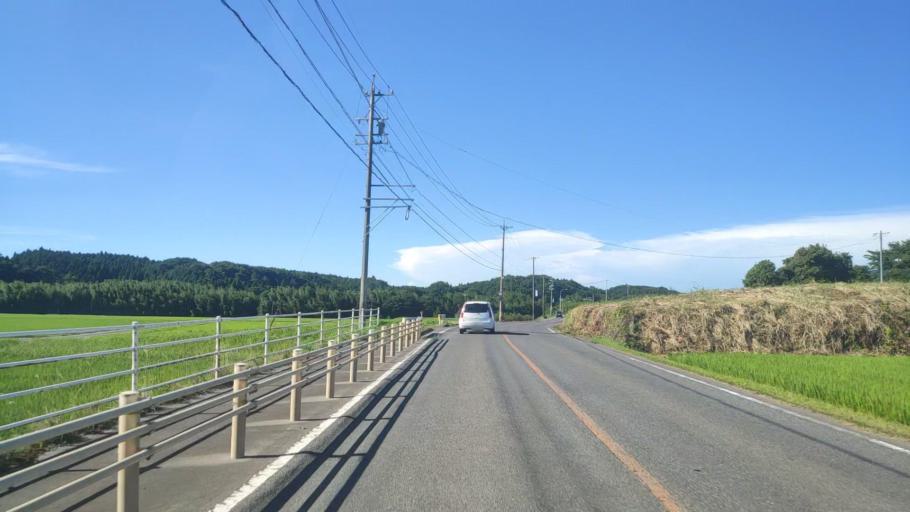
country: JP
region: Mie
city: Ueno-ebisumachi
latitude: 34.8394
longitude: 136.2352
